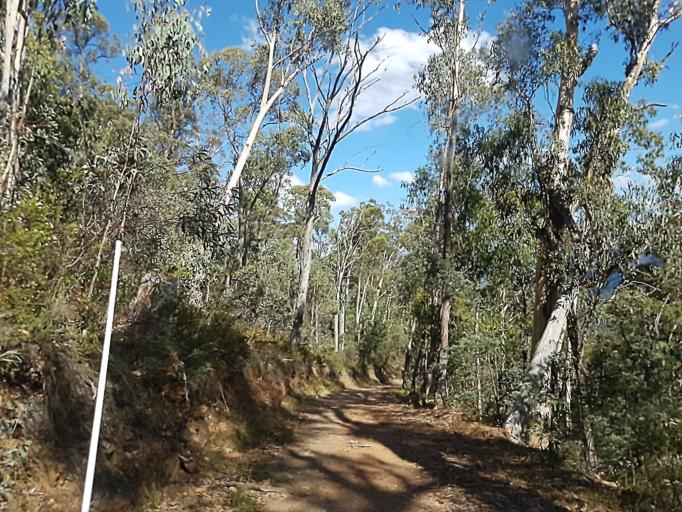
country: AU
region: Victoria
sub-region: Alpine
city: Mount Beauty
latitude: -36.8908
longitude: 147.0262
